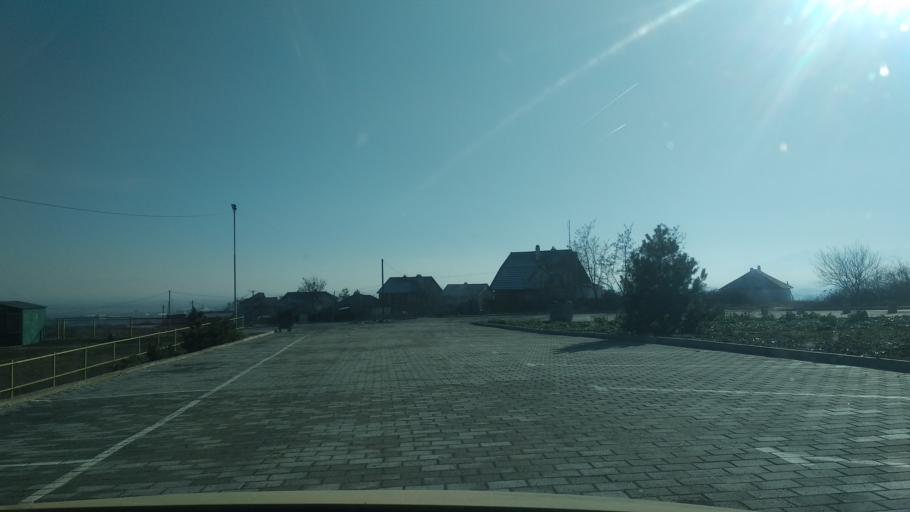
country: XK
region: Pristina
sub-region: Komuna e Gracanices
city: Glanica
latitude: 42.6098
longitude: 21.0213
